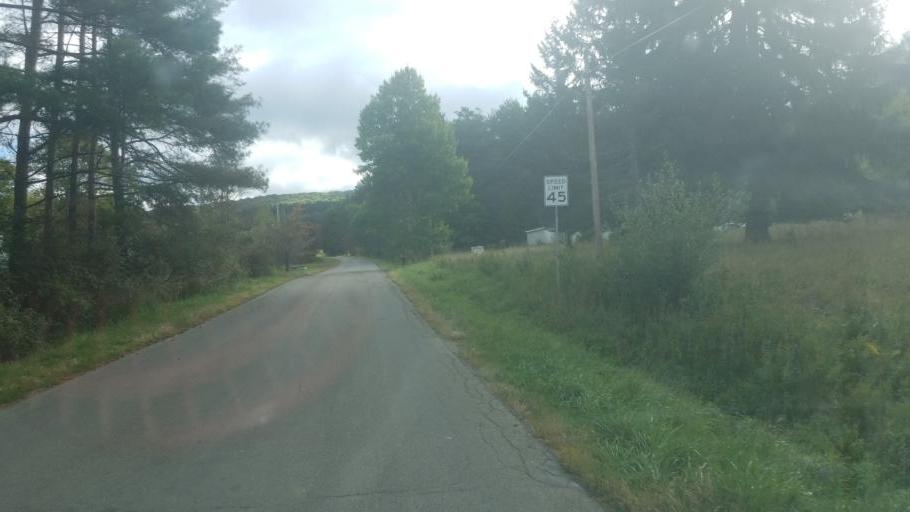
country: US
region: New York
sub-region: Cattaraugus County
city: Weston Mills
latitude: 42.1138
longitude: -78.3228
